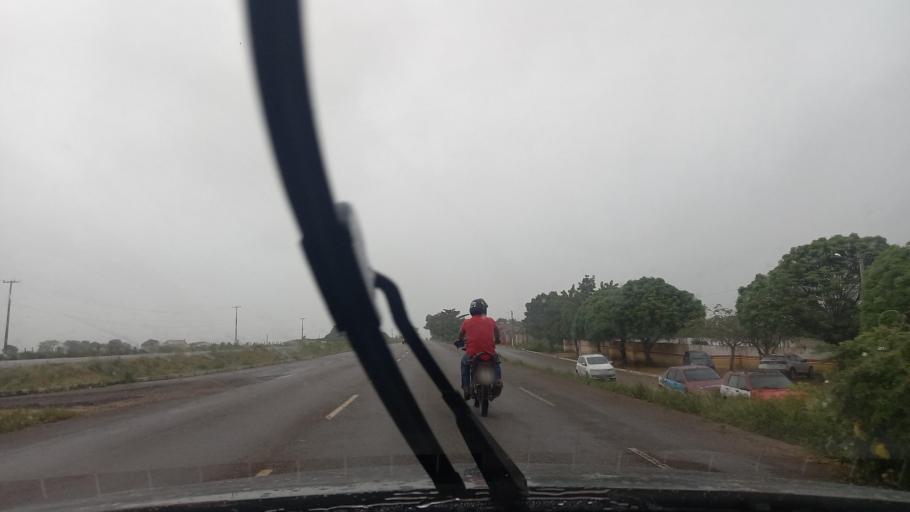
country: BR
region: Alagoas
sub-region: Lagoa Da Canoa
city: Lagoa da Canoa
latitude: -9.6998
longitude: -36.8007
